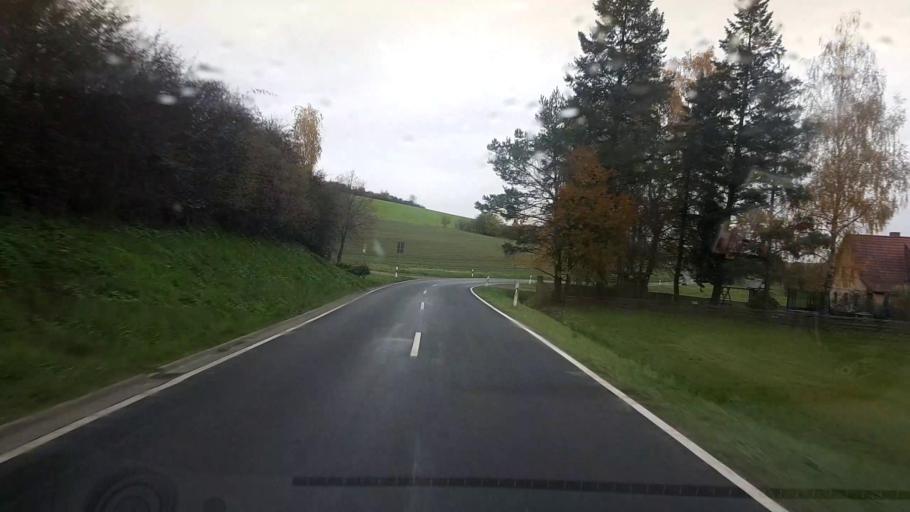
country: DE
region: Bavaria
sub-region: Upper Franconia
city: Burgwindheim
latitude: 49.8750
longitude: 10.5725
